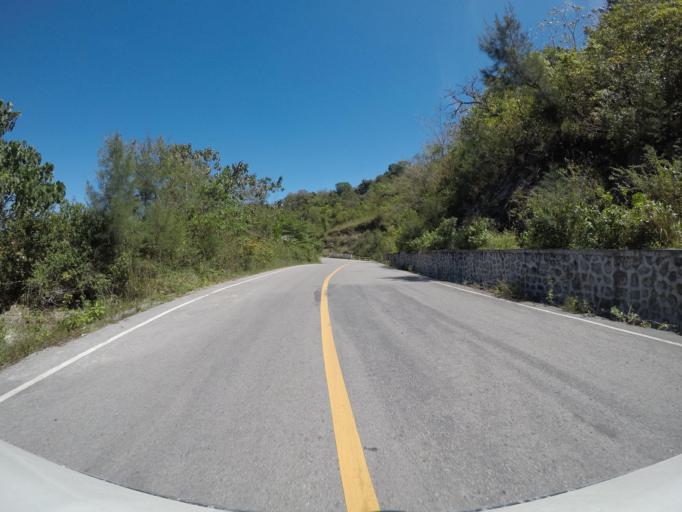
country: TL
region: Manatuto
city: Manatuto
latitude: -8.8077
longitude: 125.9733
